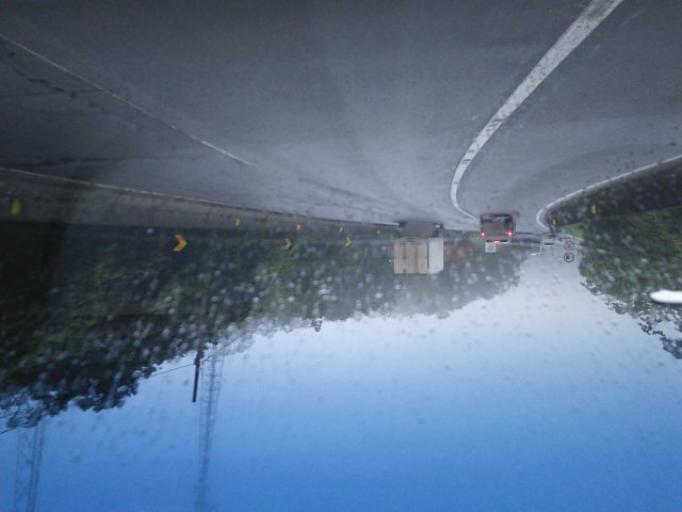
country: BR
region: Parana
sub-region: Guaratuba
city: Guaratuba
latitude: -25.8667
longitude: -48.9472
